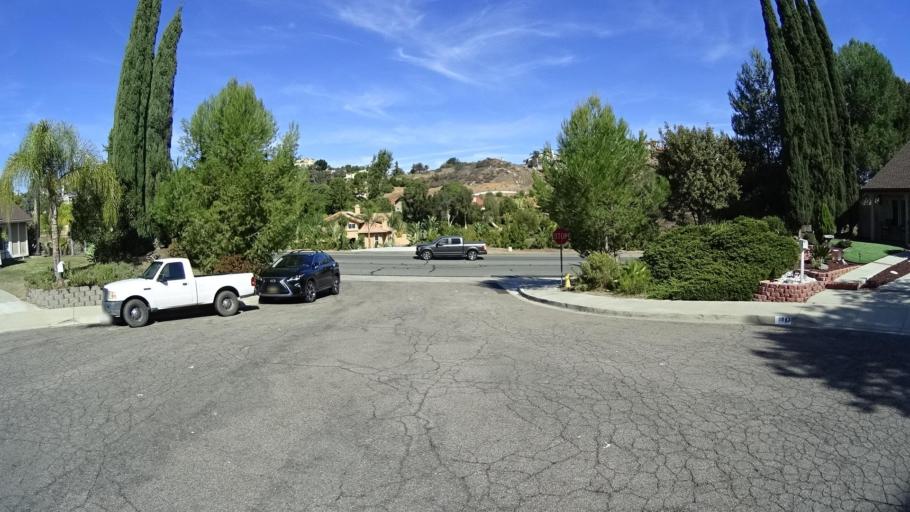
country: US
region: California
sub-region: San Diego County
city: Rancho San Diego
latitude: 32.7508
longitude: -116.9481
